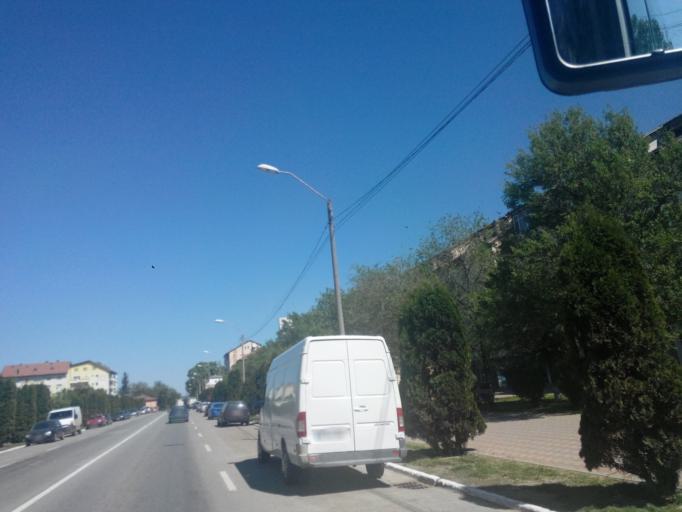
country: RO
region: Iasi
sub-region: Comuna Podu Iloaiei
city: Podu Iloaiei
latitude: 47.2116
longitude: 27.2721
